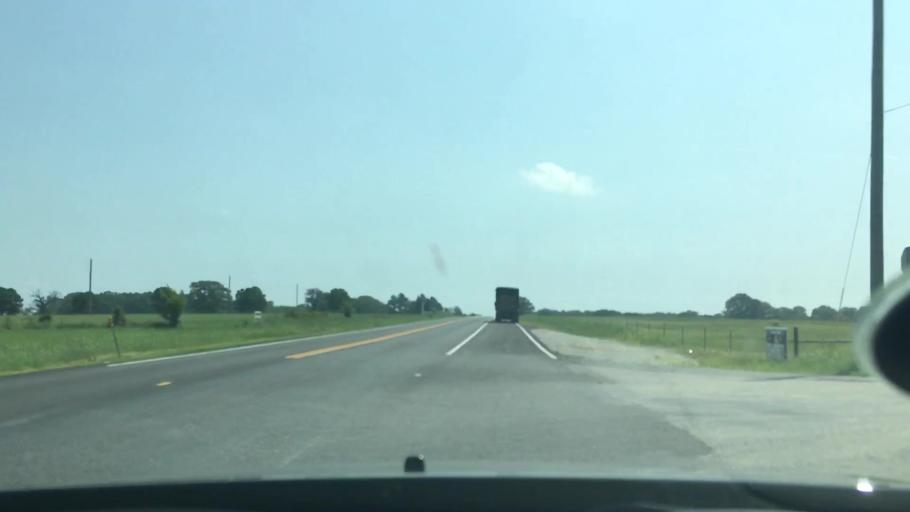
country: US
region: Oklahoma
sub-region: Atoka County
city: Atoka
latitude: 34.2782
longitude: -95.9363
